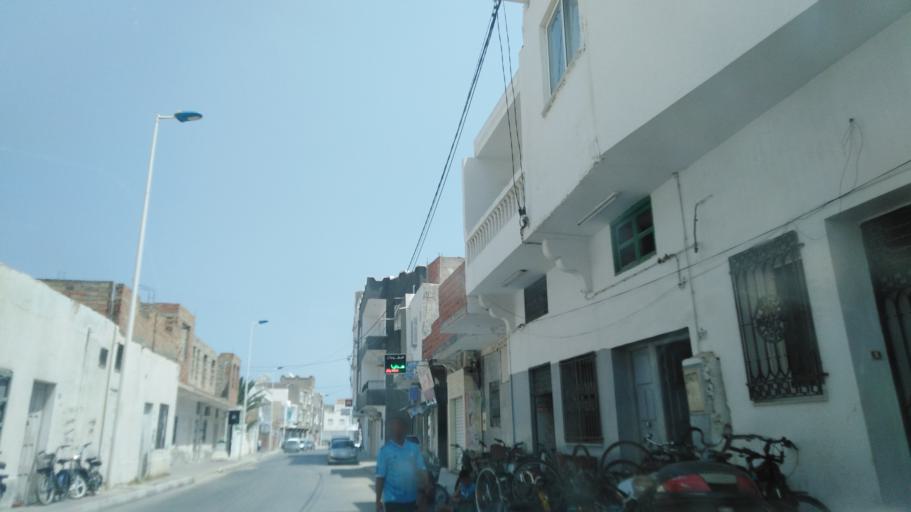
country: TN
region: Al Mahdiyah
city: Mahdia
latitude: 35.5136
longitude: 11.0437
